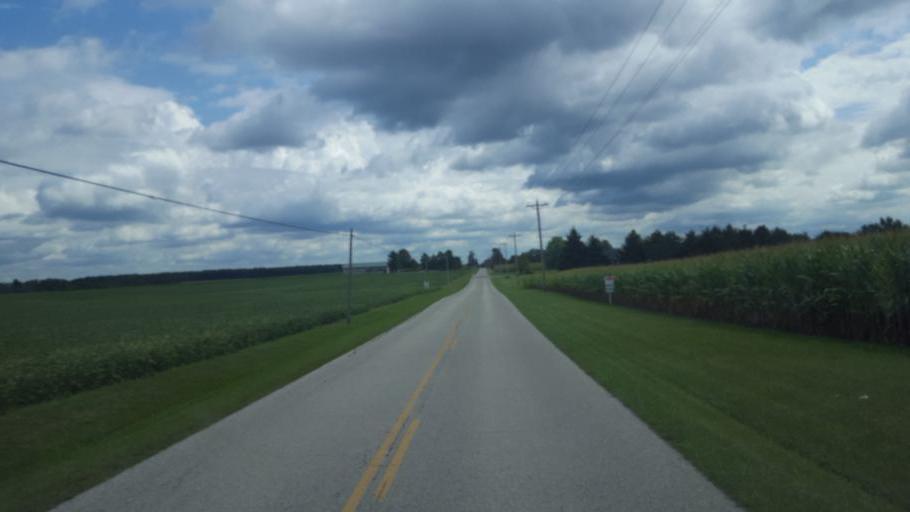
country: US
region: Ohio
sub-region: Sandusky County
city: Mount Carmel
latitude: 41.0955
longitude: -82.9274
